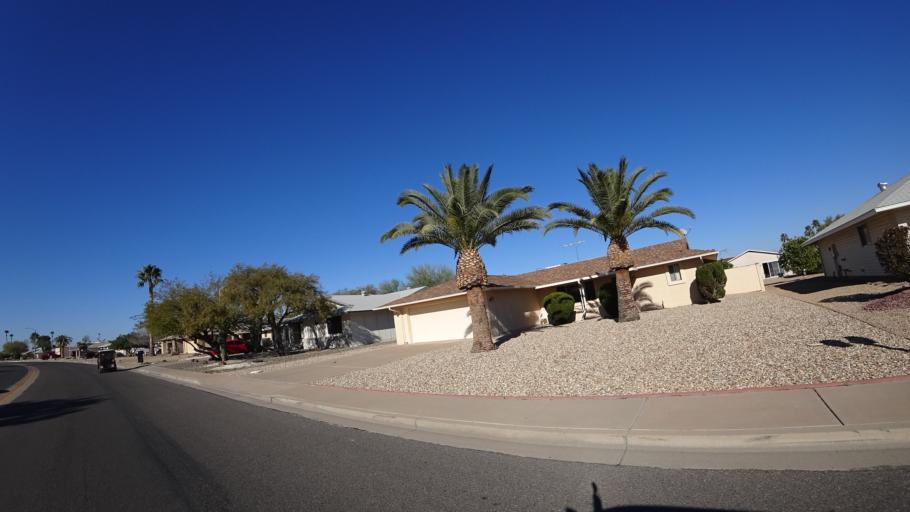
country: US
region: Arizona
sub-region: Maricopa County
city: Sun City West
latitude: 33.6676
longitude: -112.3408
